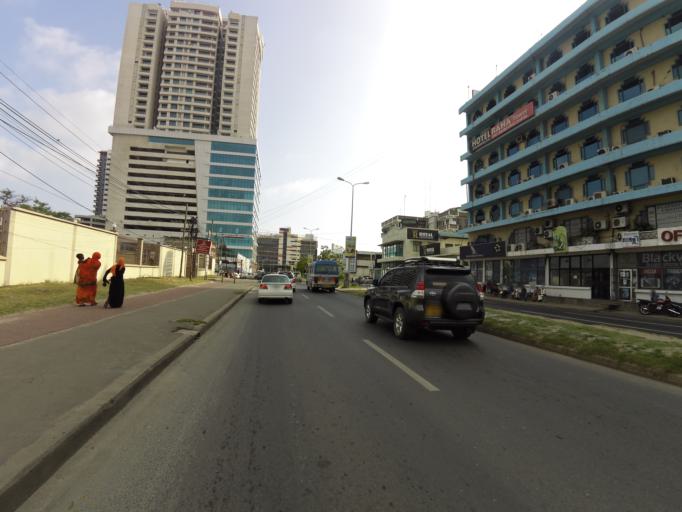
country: TZ
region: Dar es Salaam
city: Dar es Salaam
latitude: -6.8116
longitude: 39.2852
